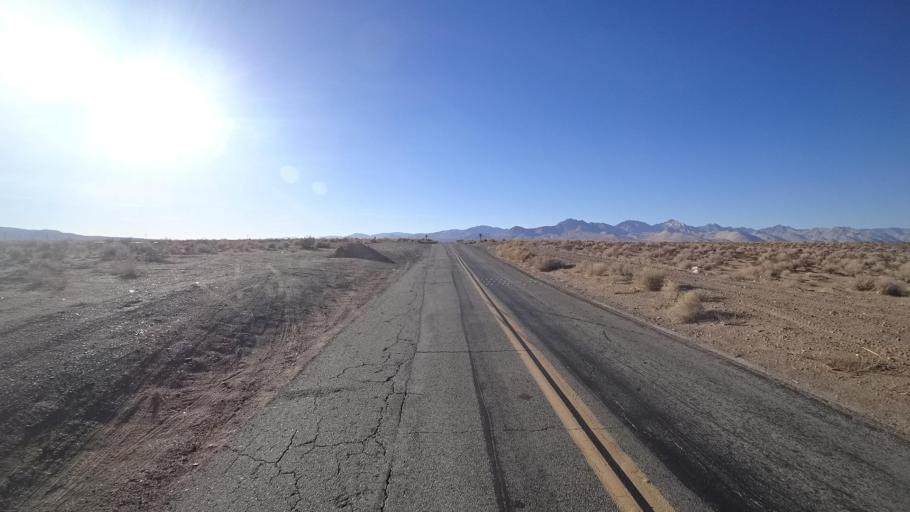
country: US
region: California
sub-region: Kern County
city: China Lake Acres
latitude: 35.6076
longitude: -117.7616
